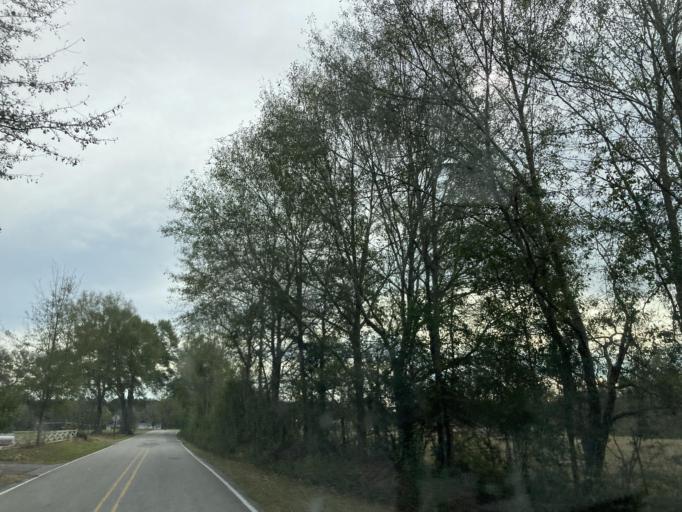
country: US
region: Mississippi
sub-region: Lamar County
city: Purvis
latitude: 31.1119
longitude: -89.4765
